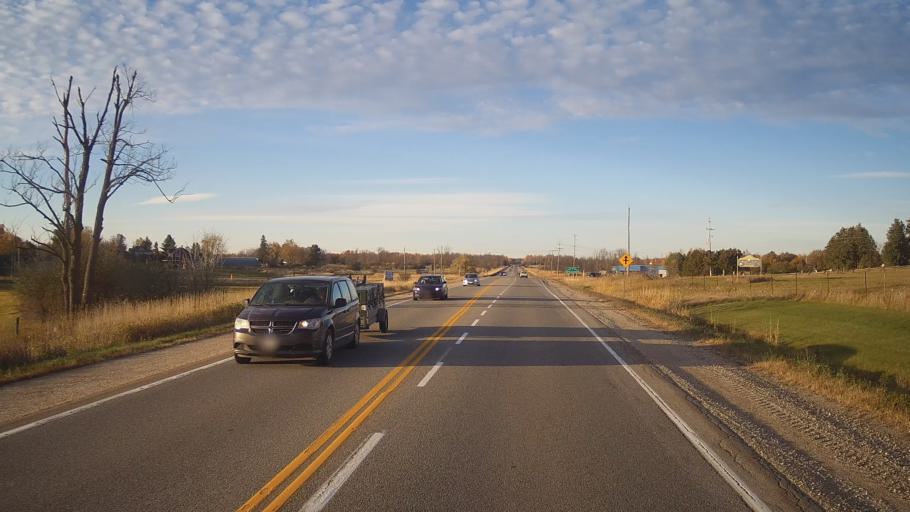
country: CA
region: Ontario
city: Perth
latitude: 44.9942
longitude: -76.2283
